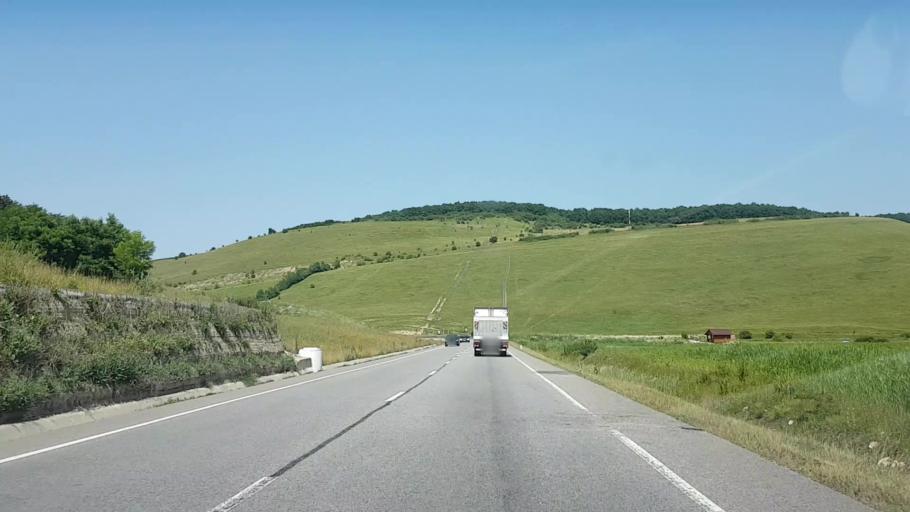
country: RO
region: Cluj
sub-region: Comuna Apahida
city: Dezmir
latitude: 46.7420
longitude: 23.7104
